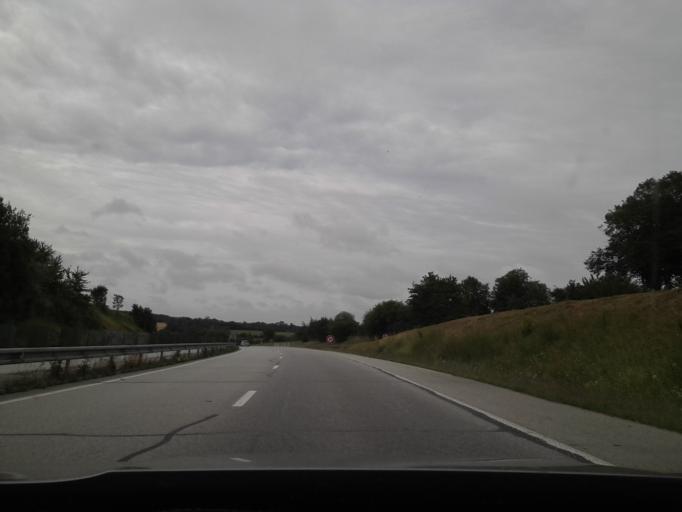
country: FR
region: Lower Normandy
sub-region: Departement de la Manche
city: Sainte-Mere-Eglise
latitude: 49.3962
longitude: -1.3070
